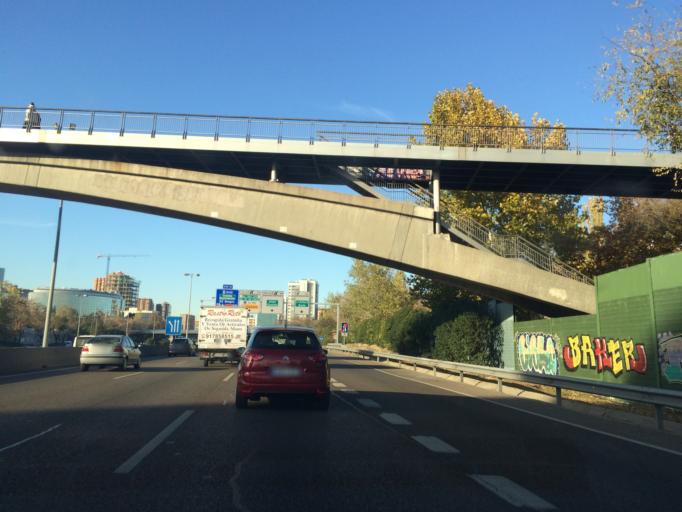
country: ES
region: Madrid
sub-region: Provincia de Madrid
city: Chamartin
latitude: 40.4637
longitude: -3.6664
